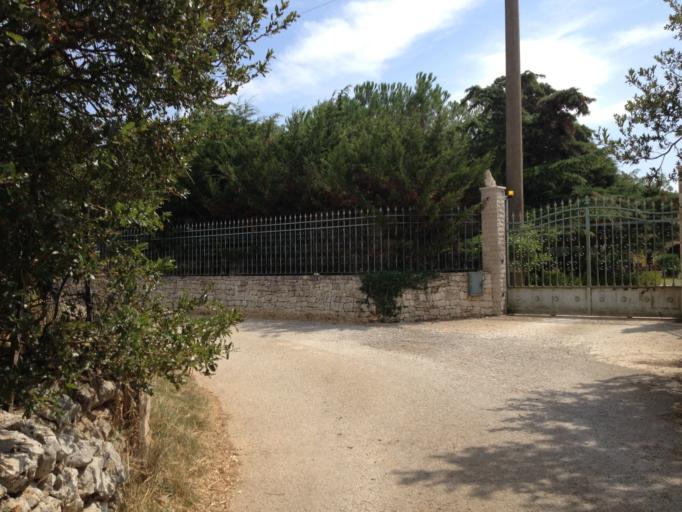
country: IT
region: Apulia
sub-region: Provincia di Bari
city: Gioia del Colle
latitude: 40.8252
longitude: 16.9818
